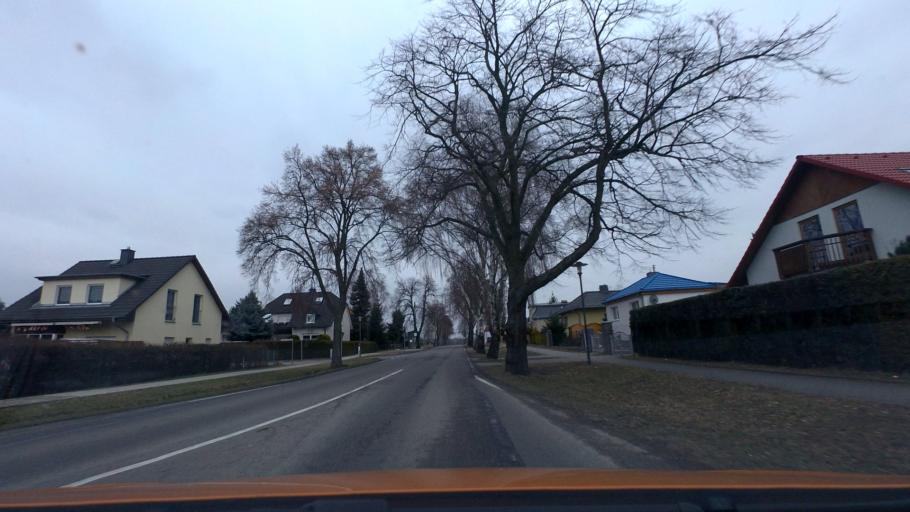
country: DE
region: Brandenburg
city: Ahrensfelde
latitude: 52.5684
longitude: 13.5903
